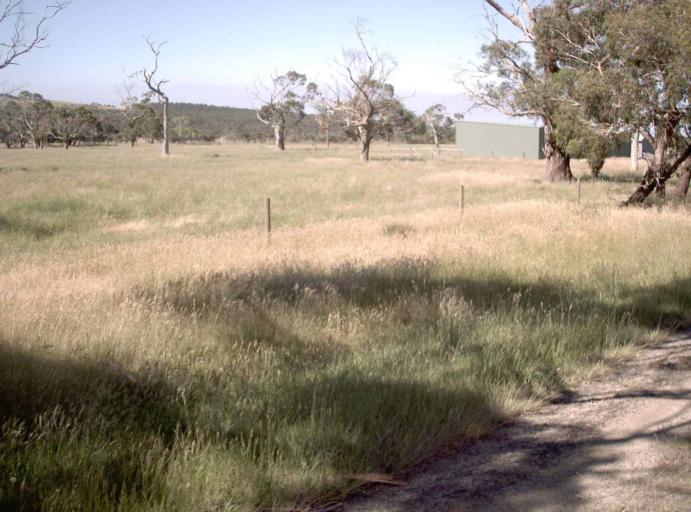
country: AU
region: Victoria
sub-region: Latrobe
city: Morwell
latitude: -38.6321
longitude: 146.5574
